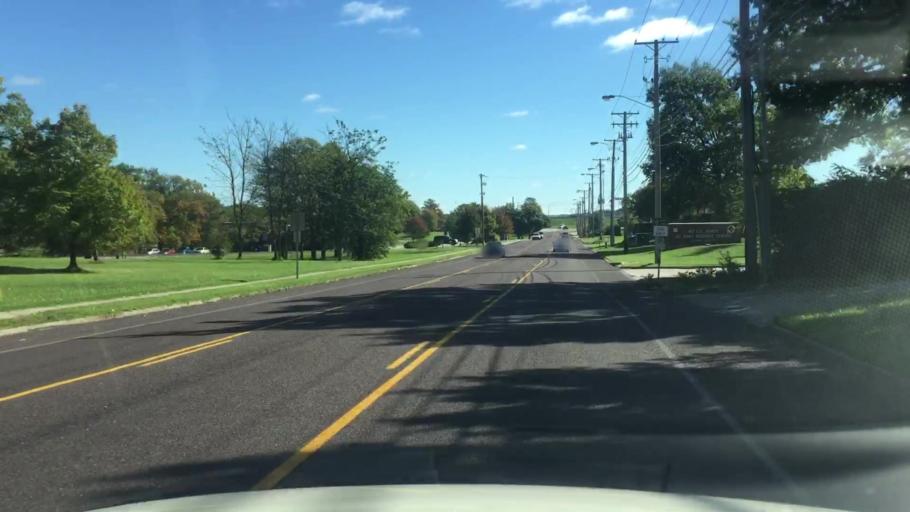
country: US
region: Missouri
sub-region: Boone County
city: Columbia
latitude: 38.9672
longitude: -92.3584
